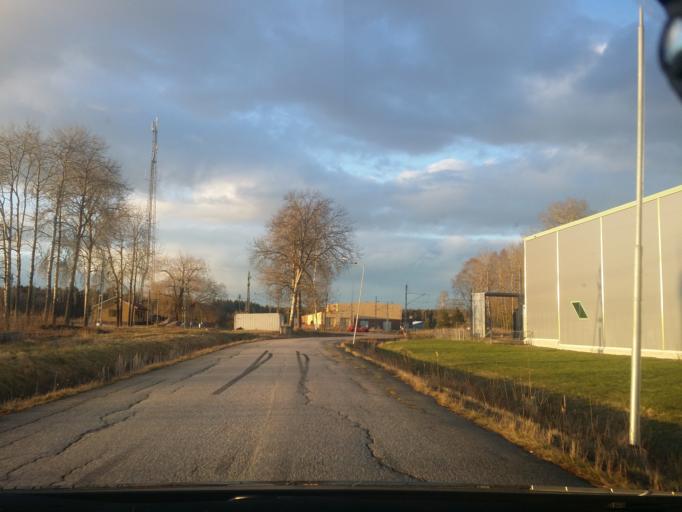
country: SE
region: Vaestmanland
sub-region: Vasteras
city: Hokasen
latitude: 59.6479
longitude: 16.5861
